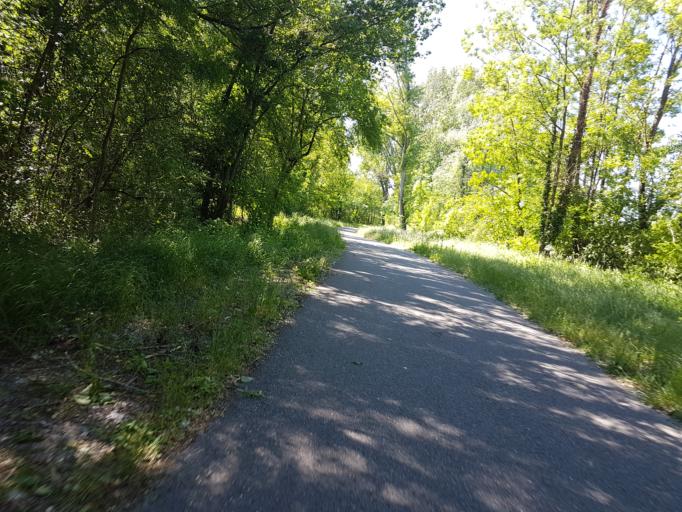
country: FR
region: Rhone-Alpes
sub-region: Departement de la Drome
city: Andancette
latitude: 45.2644
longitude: 4.8120
